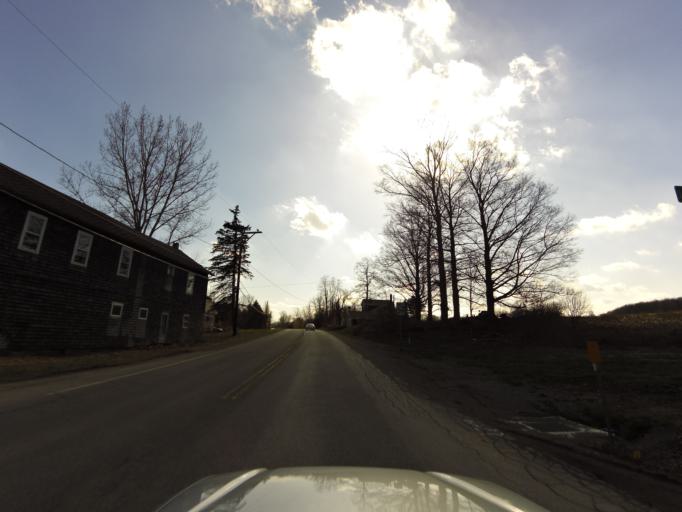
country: US
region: New York
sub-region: Wyoming County
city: Castile
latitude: 42.5914
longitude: -78.1061
